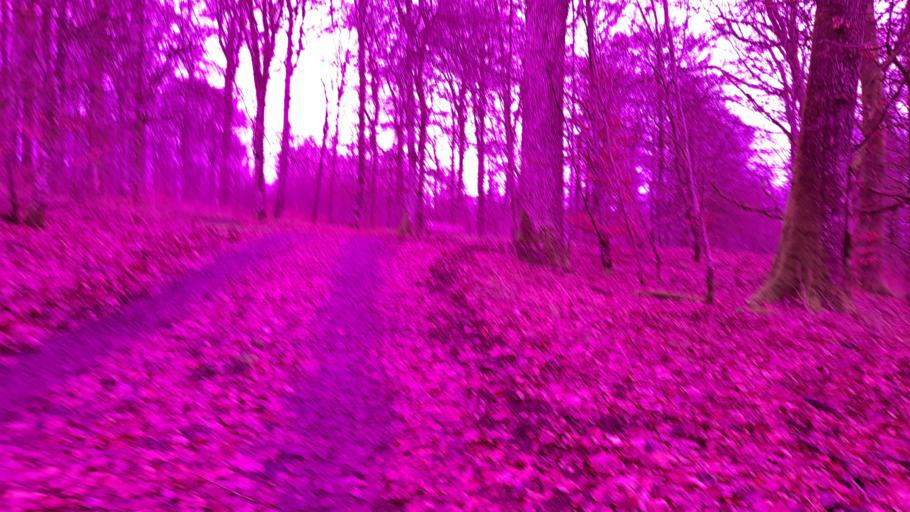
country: DE
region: Rheinland-Pfalz
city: Dasburg
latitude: 50.0689
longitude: 6.1192
